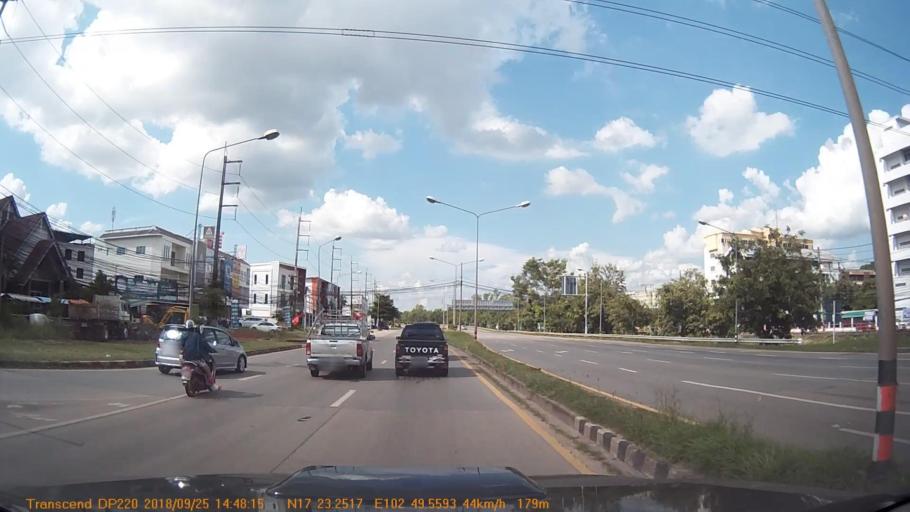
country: TH
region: Changwat Udon Thani
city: Udon Thani
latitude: 17.3879
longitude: 102.8260
